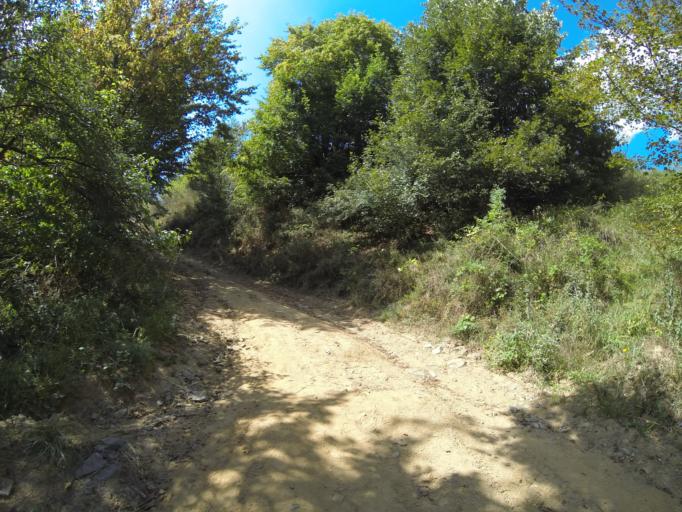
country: RO
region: Mehedinti
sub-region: Comuna Svinita
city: Svinita
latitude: 44.5530
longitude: 22.1360
